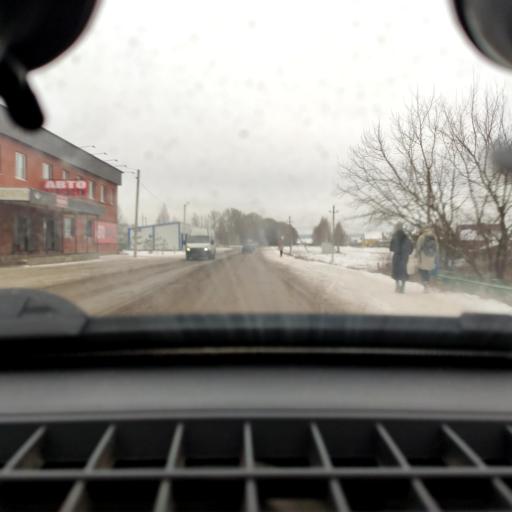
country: RU
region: Bashkortostan
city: Iglino
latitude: 54.8126
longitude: 56.4082
